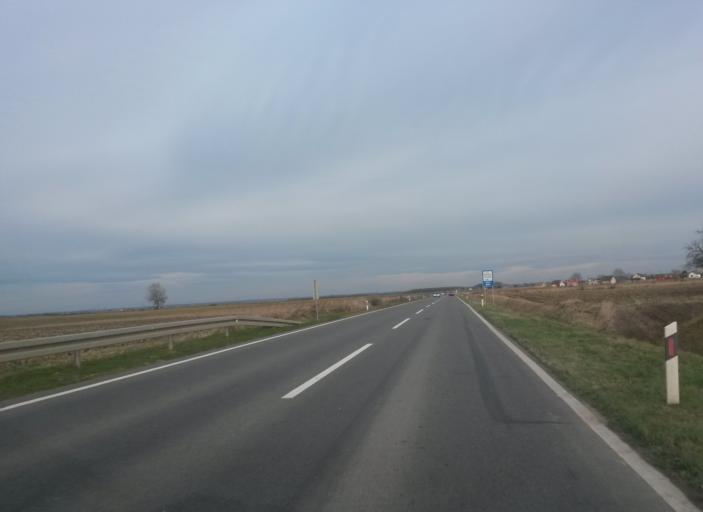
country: HR
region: Osjecko-Baranjska
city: Cepin
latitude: 45.5264
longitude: 18.5422
